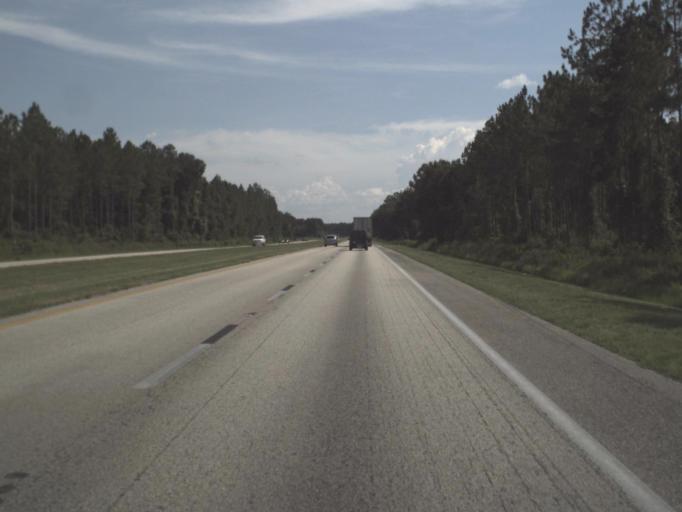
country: US
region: Florida
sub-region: Marion County
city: Citra
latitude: 29.4853
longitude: -82.1023
